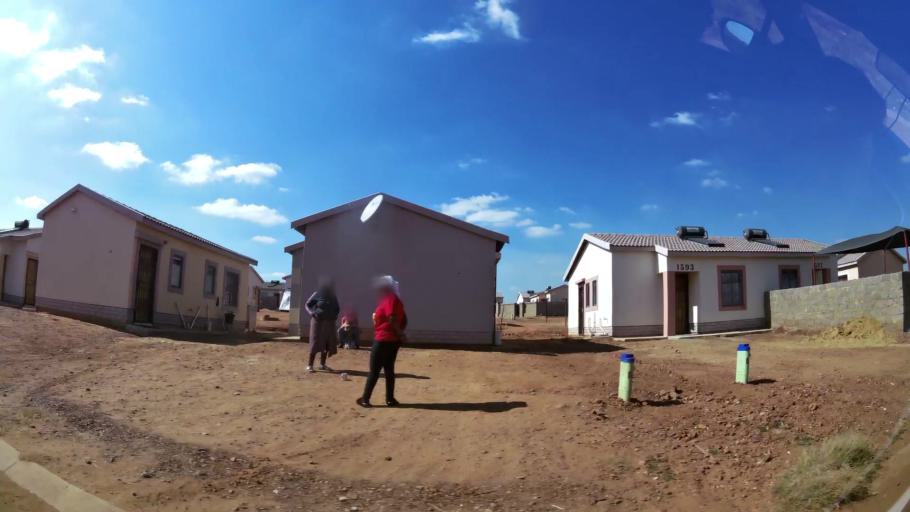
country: ZA
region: Gauteng
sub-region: West Rand District Municipality
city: Randfontein
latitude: -26.1709
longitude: 27.7694
